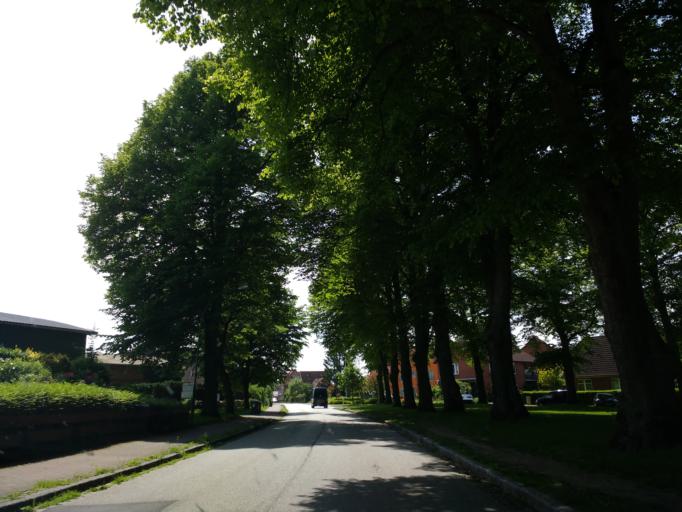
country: DE
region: Schleswig-Holstein
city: Siek
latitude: 53.6334
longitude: 10.2980
